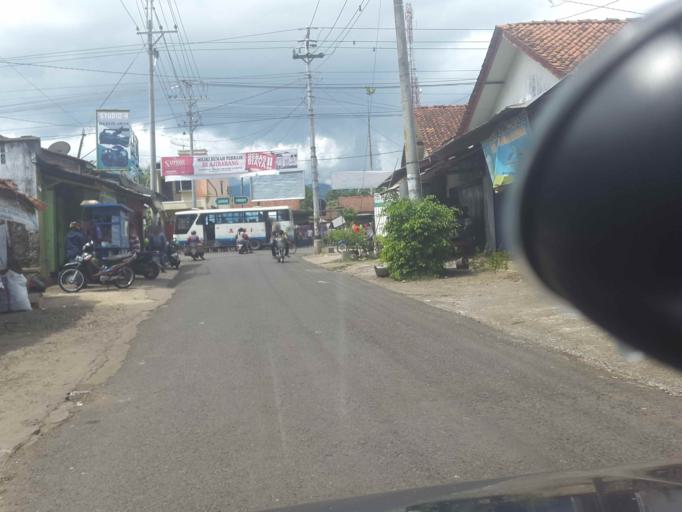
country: ID
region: Central Java
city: Purwokerto
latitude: -7.4050
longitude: 109.1401
